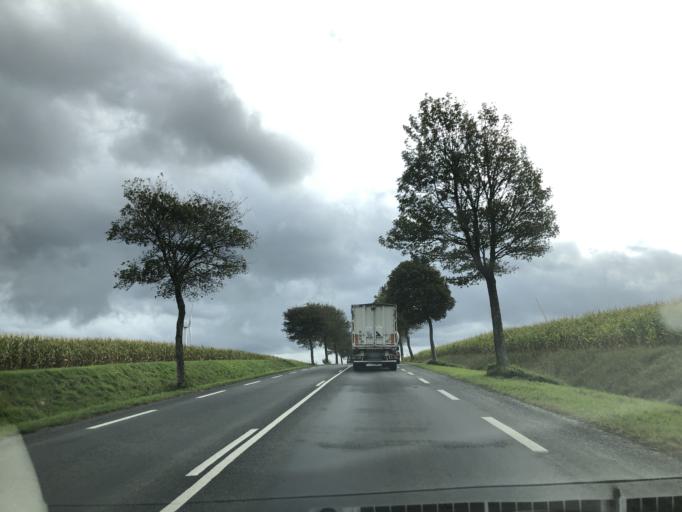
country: FR
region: Nord-Pas-de-Calais
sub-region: Departement du Pas-de-Calais
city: Wailly
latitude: 50.5743
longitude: 2.0959
